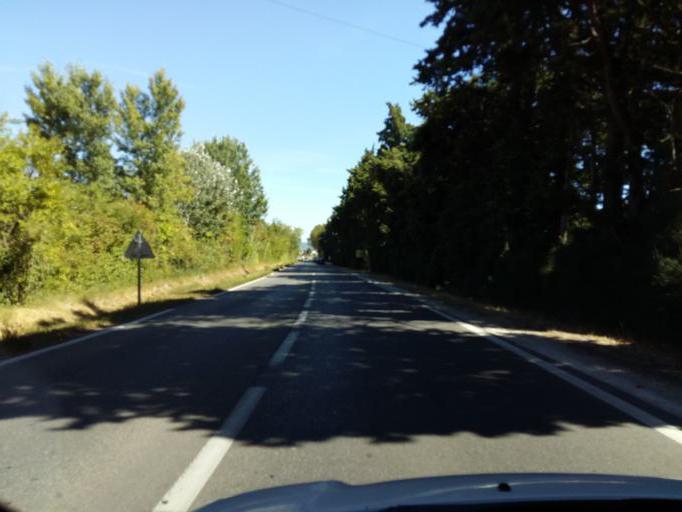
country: FR
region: Provence-Alpes-Cote d'Azur
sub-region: Departement du Vaucluse
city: Le Thor
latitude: 43.9213
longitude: 5.0215
